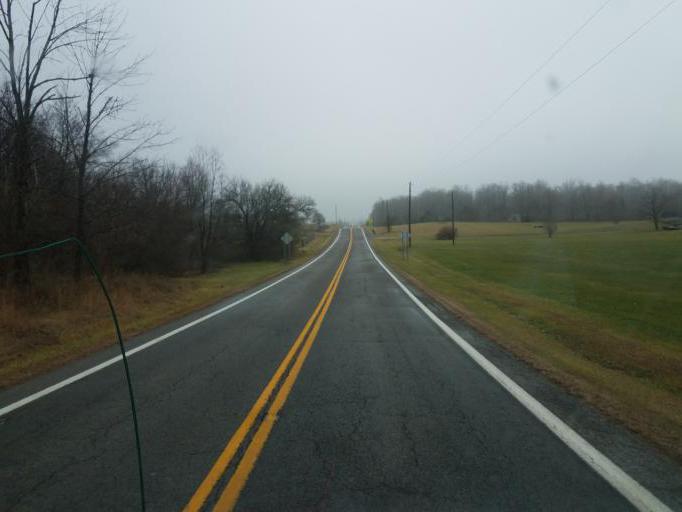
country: US
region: Ohio
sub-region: Champaign County
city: North Lewisburg
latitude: 40.2773
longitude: -83.6002
